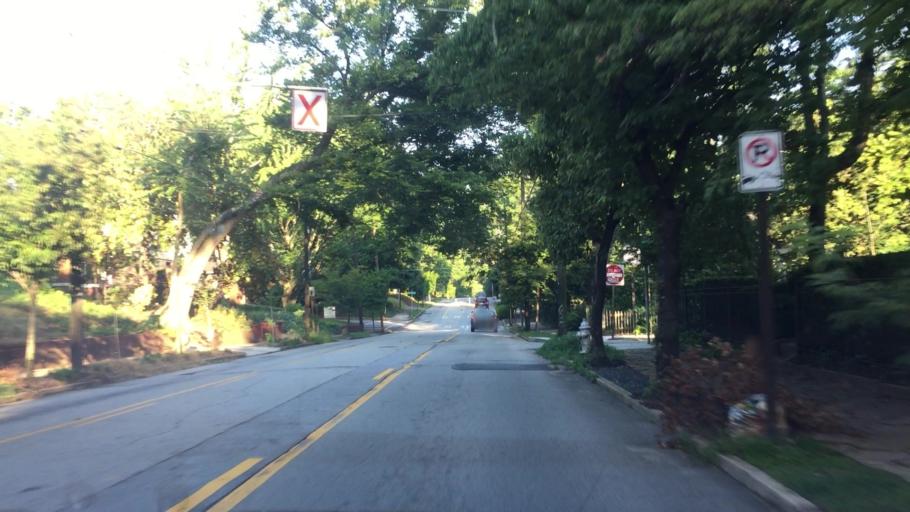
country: US
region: Georgia
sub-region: DeKalb County
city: Druid Hills
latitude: 33.7711
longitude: -84.3534
